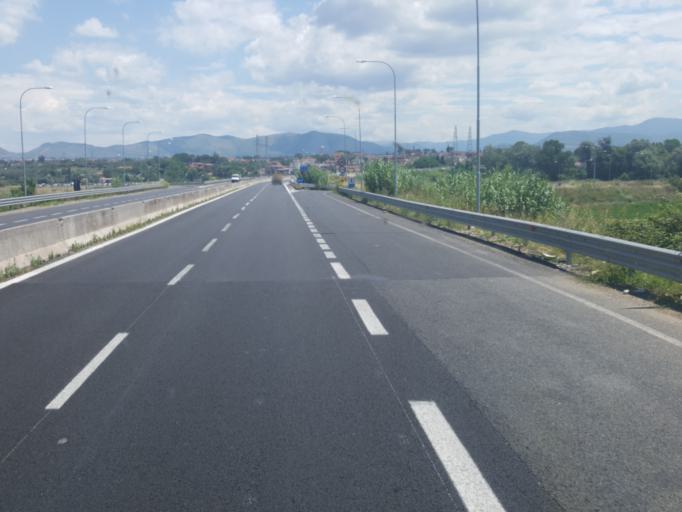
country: IT
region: Latium
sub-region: Citta metropolitana di Roma Capitale
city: Fiano Romano
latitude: 42.1521
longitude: 12.6387
